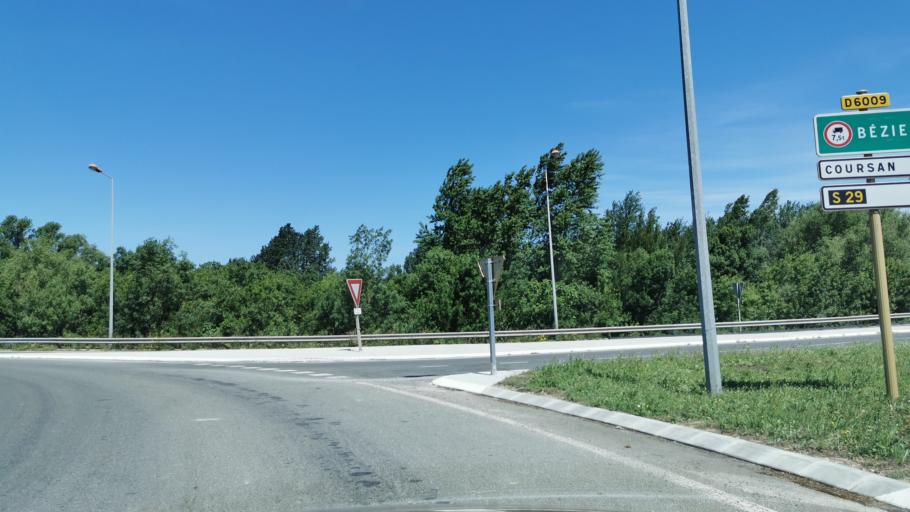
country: FR
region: Languedoc-Roussillon
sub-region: Departement de l'Aude
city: Narbonne
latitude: 43.2011
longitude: 3.0198
